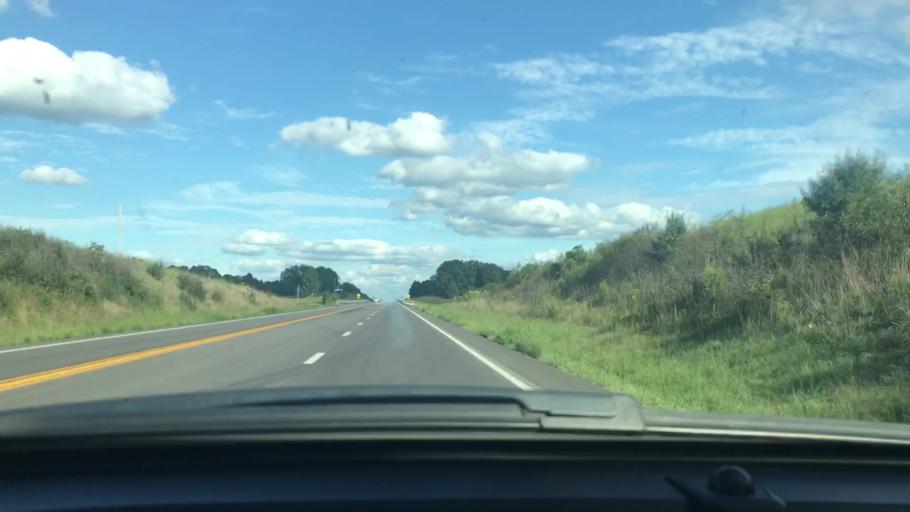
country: US
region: Missouri
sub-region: Oregon County
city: Thayer
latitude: 36.5849
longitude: -91.6193
